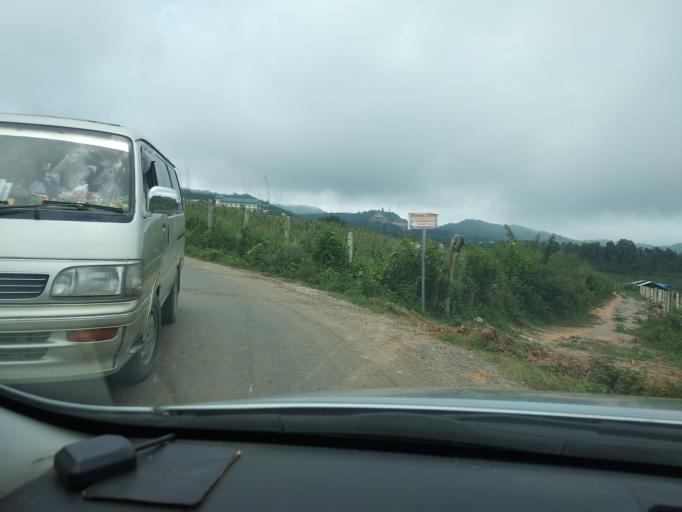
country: MM
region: Mandalay
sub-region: Pyin Oo Lwin District
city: Pyin Oo Lwin
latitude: 21.9184
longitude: 96.3818
